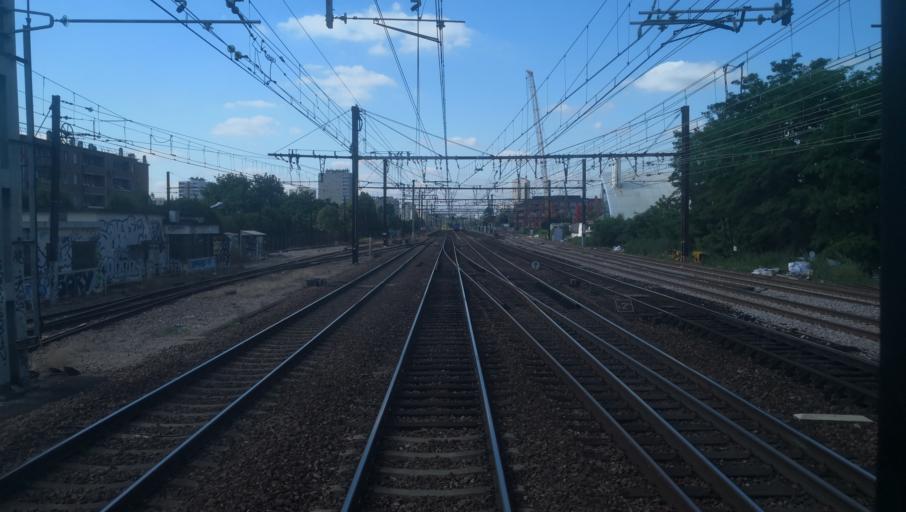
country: FR
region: Ile-de-France
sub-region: Departement du Val-de-Marne
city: Choisy-le-Roi
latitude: 48.7862
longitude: 2.4330
